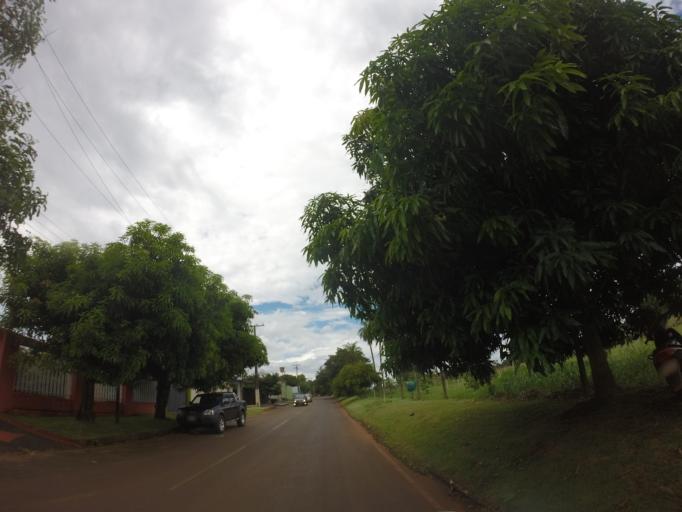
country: PY
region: Alto Parana
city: Ciudad del Este
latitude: -25.4084
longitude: -54.6223
